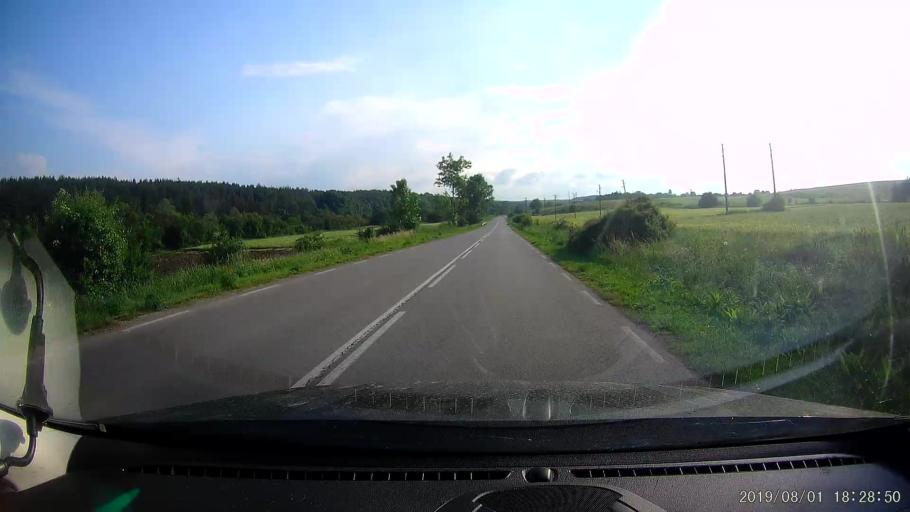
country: BG
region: Shumen
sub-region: Obshtina Venets
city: Venets
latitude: 43.5695
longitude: 26.9555
